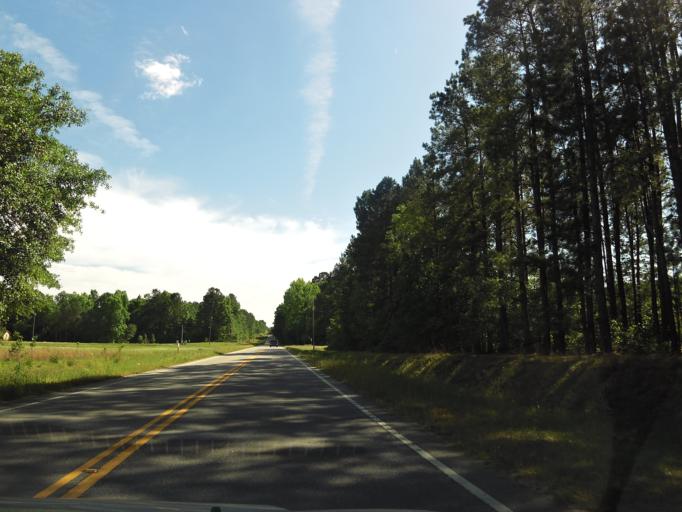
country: US
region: South Carolina
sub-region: Bamberg County
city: Denmark
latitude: 33.2838
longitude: -81.1501
